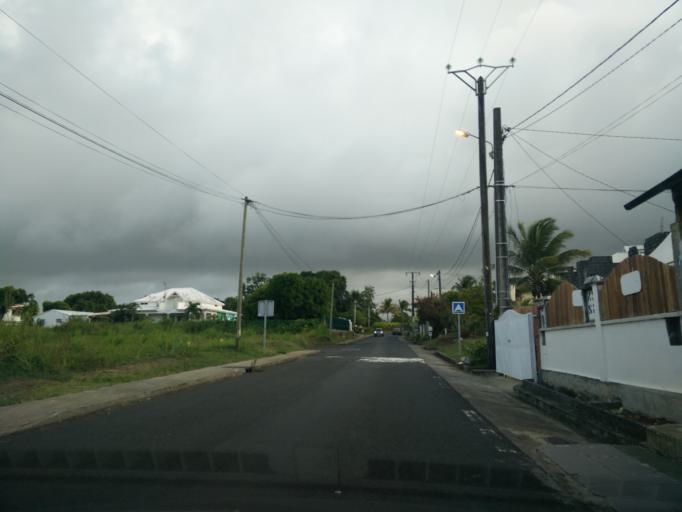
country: GP
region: Guadeloupe
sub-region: Guadeloupe
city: Petit-Bourg
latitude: 16.1913
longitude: -61.6099
